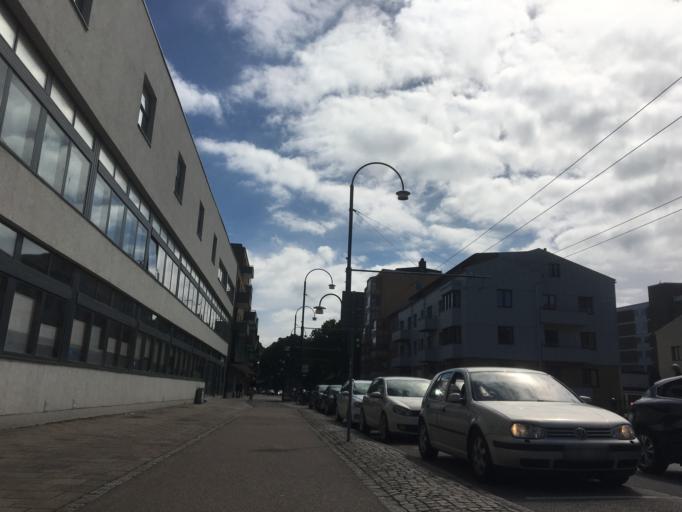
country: SE
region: Skane
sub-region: Landskrona
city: Landskrona
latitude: 55.8756
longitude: 12.8323
